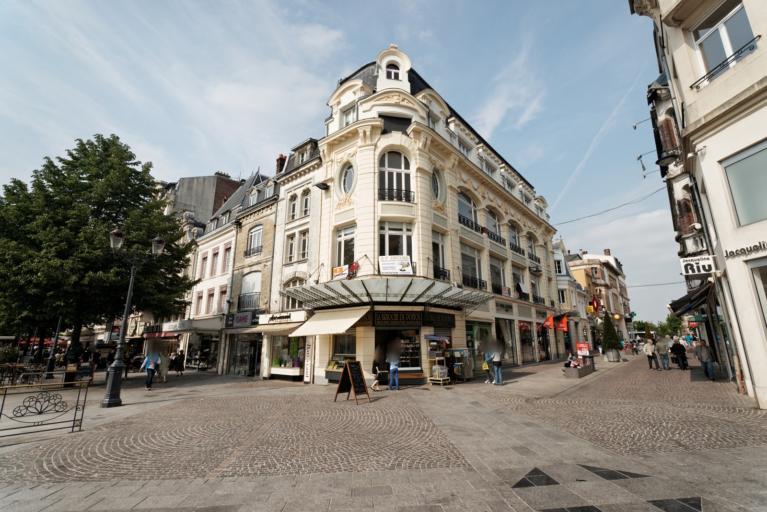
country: FR
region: Picardie
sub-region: Departement de l'Aisne
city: Saint-Quentin
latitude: 49.8464
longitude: 3.2884
